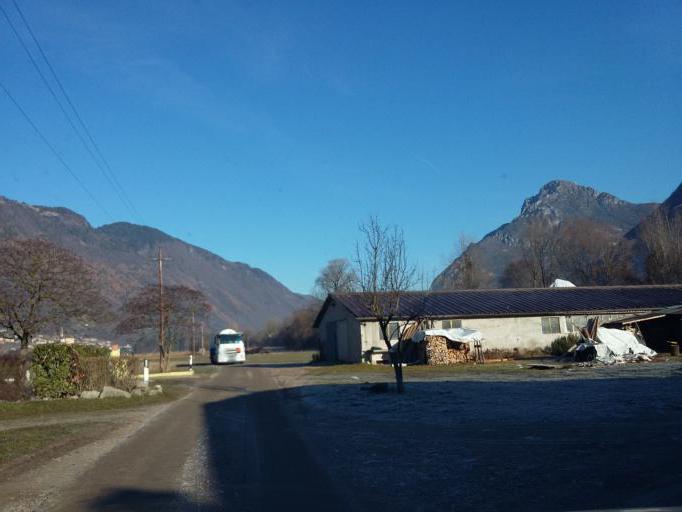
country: IT
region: Trentino-Alto Adige
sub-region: Provincia di Trento
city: Lodrone-Darzo
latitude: 45.8260
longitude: 10.5484
